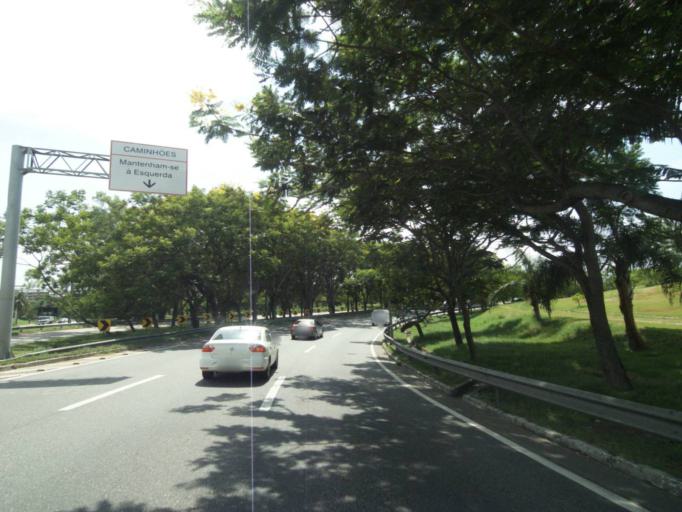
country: BR
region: Rio de Janeiro
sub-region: Rio De Janeiro
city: Rio de Janeiro
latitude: -22.8606
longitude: -43.2348
